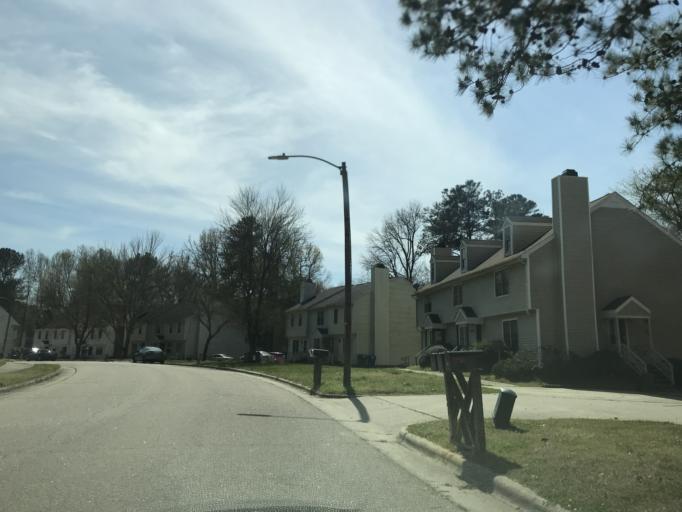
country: US
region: North Carolina
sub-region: Wake County
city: Raleigh
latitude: 35.8409
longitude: -78.5964
